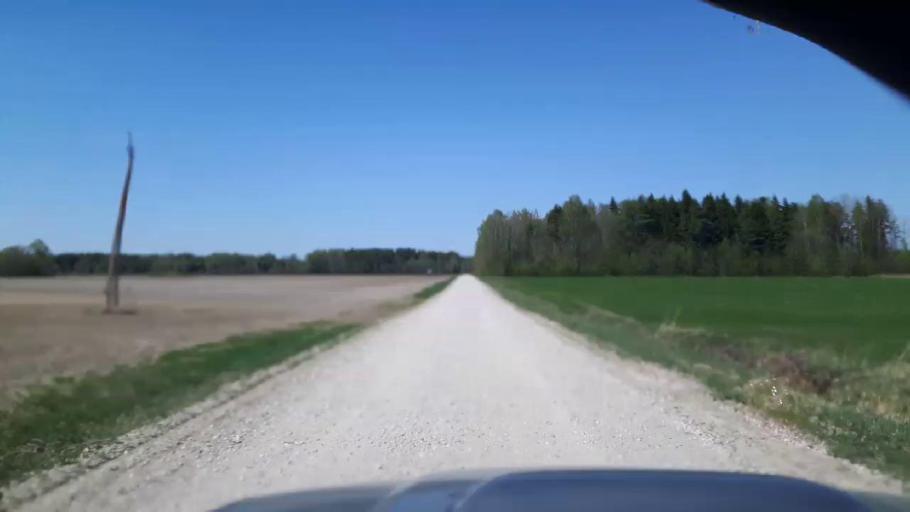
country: EE
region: Paernumaa
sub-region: Tootsi vald
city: Tootsi
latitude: 58.4698
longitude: 24.7715
